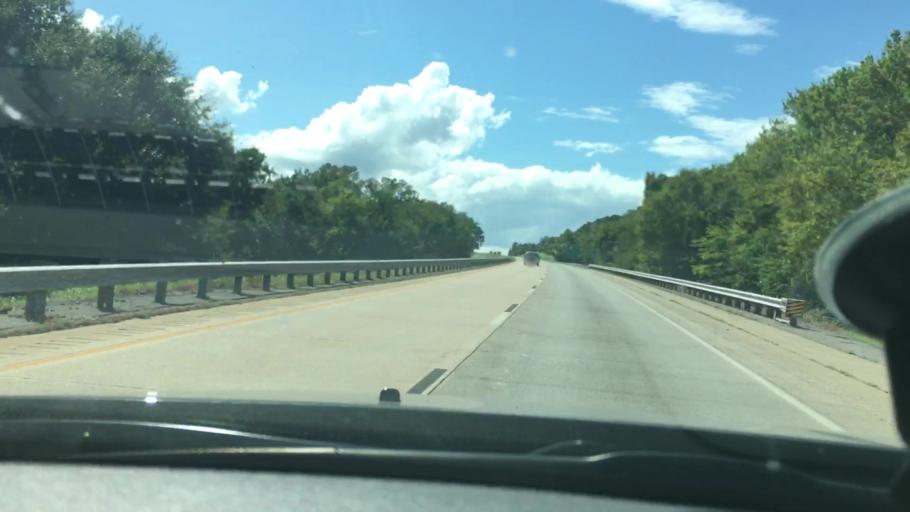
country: US
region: Oklahoma
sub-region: Sequoyah County
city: Vian
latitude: 35.4918
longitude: -95.0545
